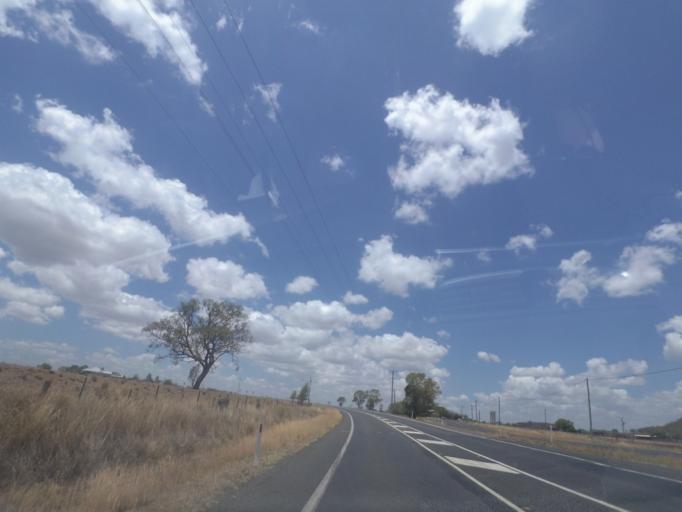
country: AU
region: Queensland
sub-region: Toowoomba
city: Top Camp
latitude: -27.7317
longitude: 151.9122
